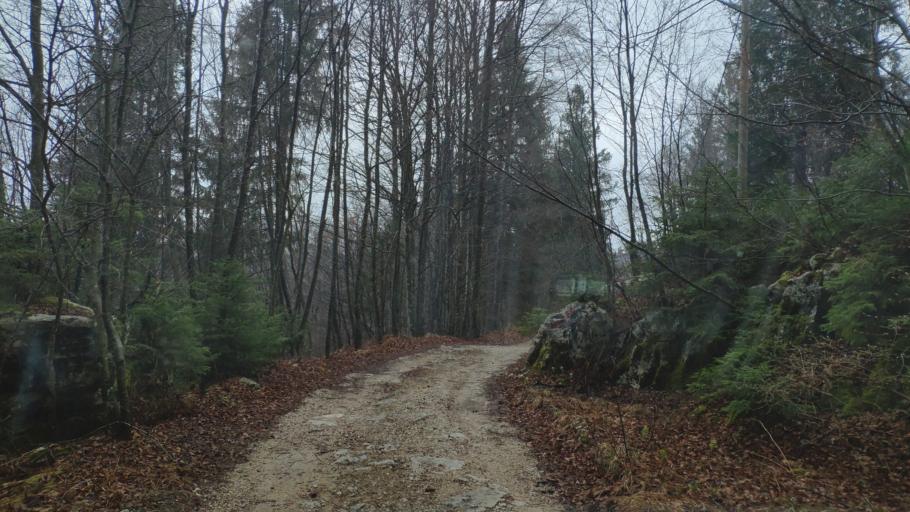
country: IT
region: Veneto
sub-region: Provincia di Vicenza
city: Rotzo
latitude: 45.8206
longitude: 11.3979
